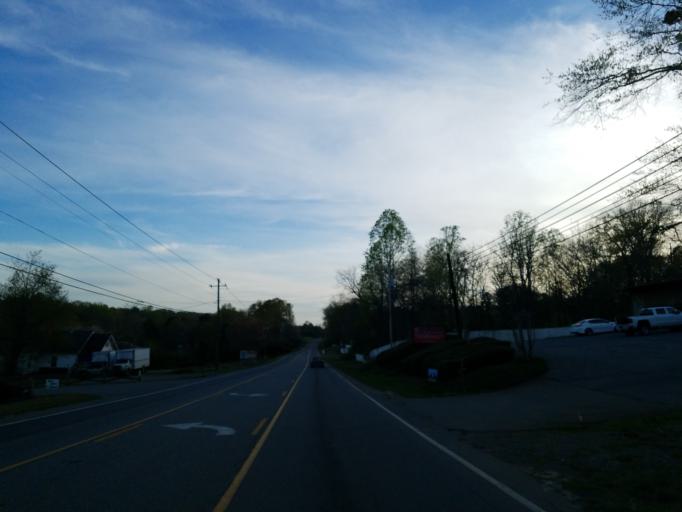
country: US
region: Georgia
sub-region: Cherokee County
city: Canton
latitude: 34.2734
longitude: -84.4527
